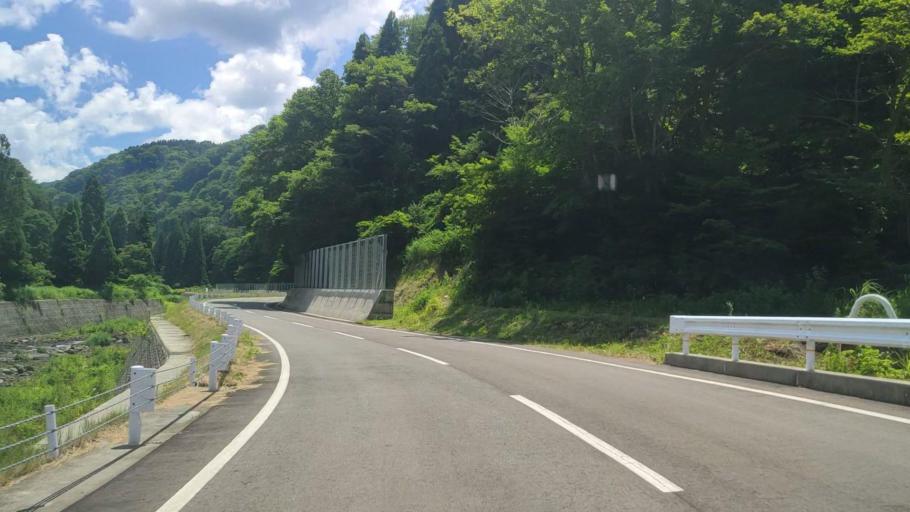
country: JP
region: Fukui
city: Ono
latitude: 35.8279
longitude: 136.4451
